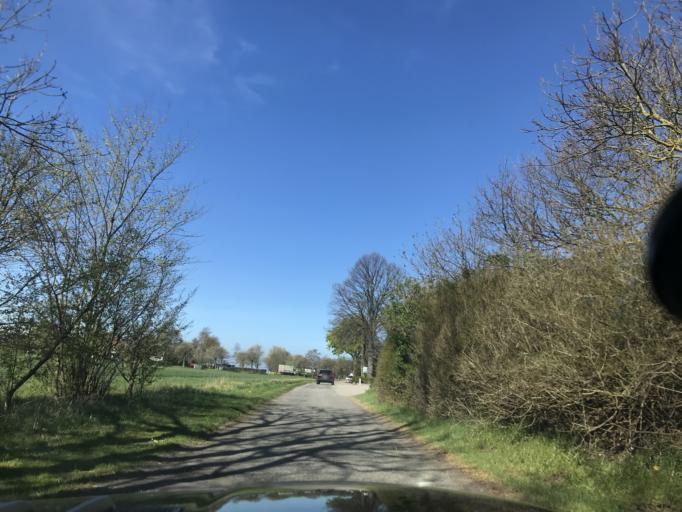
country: DE
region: Schleswig-Holstein
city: Grossenbrode
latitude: 54.4571
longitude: 11.0476
